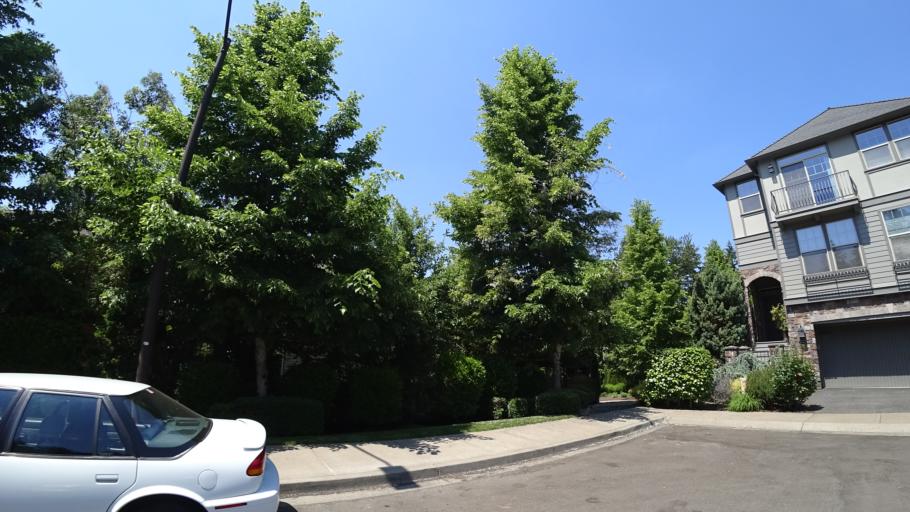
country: US
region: Oregon
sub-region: Washington County
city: Metzger
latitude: 45.4296
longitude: -122.7248
